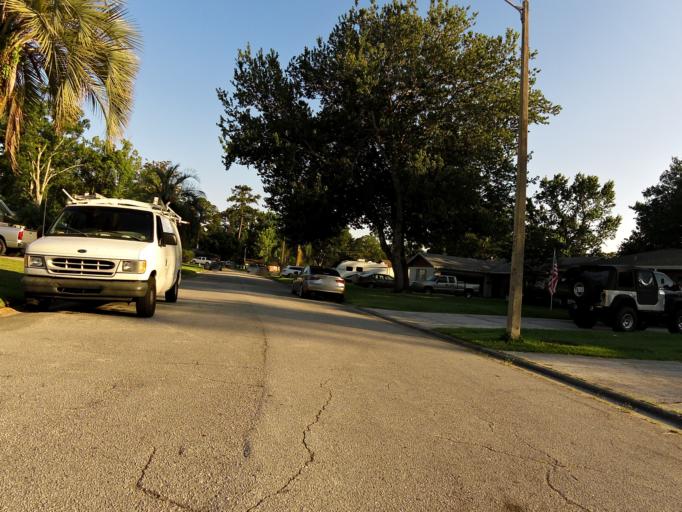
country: US
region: Florida
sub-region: Duval County
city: Jacksonville
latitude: 30.2369
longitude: -81.6022
